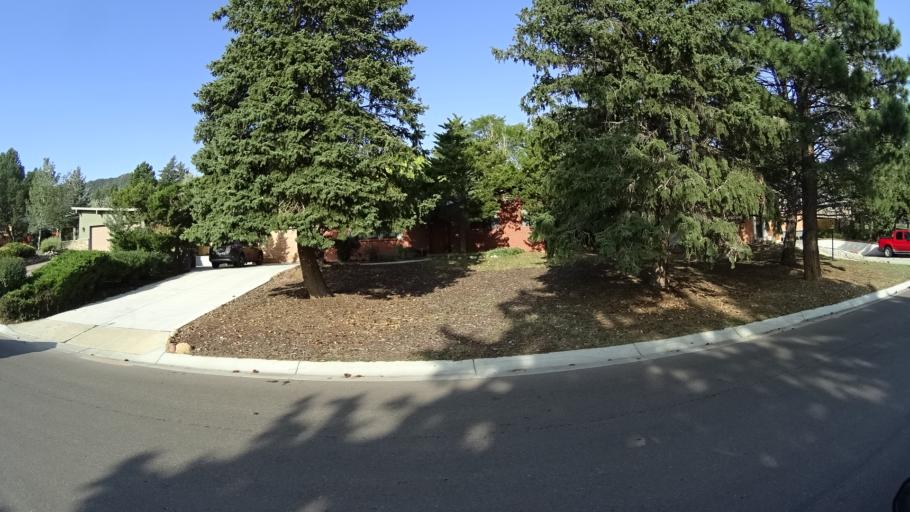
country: US
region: Colorado
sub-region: El Paso County
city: Colorado Springs
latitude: 38.8205
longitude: -104.8645
